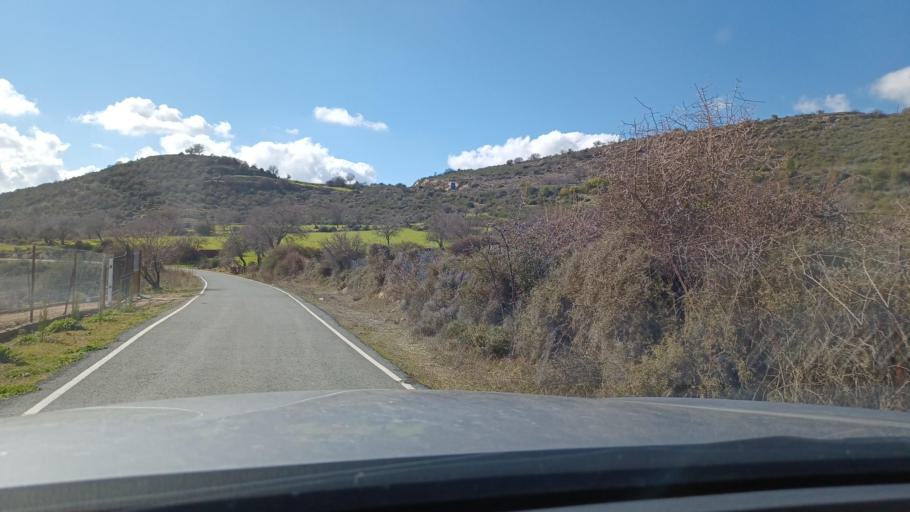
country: CY
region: Limassol
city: Pachna
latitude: 34.8302
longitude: 32.8081
